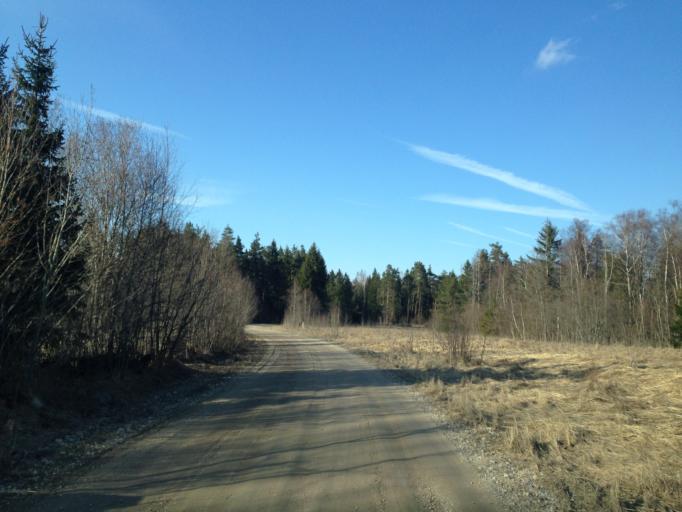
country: EE
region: Harju
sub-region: Nissi vald
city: Turba
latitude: 59.1171
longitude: 24.1611
